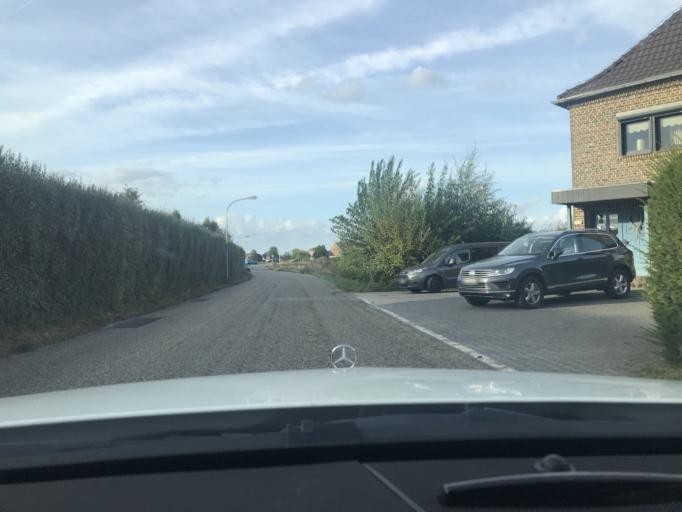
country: DE
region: North Rhine-Westphalia
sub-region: Regierungsbezirk Dusseldorf
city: Neubrueck
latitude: 51.1297
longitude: 6.6797
